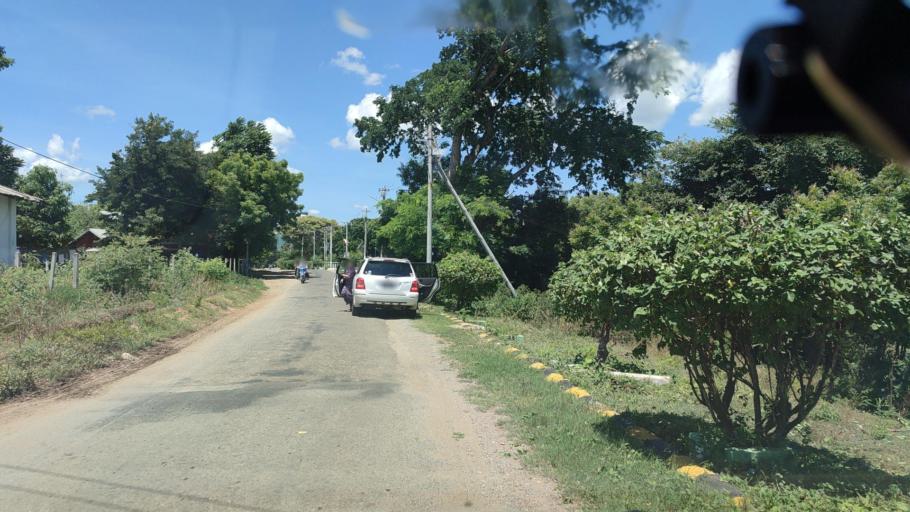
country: MM
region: Magway
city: Myaydo
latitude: 19.7279
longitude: 95.1675
